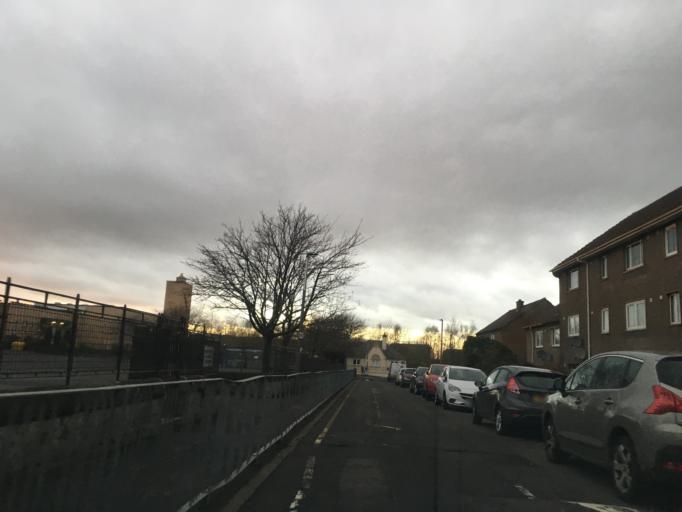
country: GB
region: Scotland
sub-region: Edinburgh
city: Colinton
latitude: 55.9214
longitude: -3.2604
